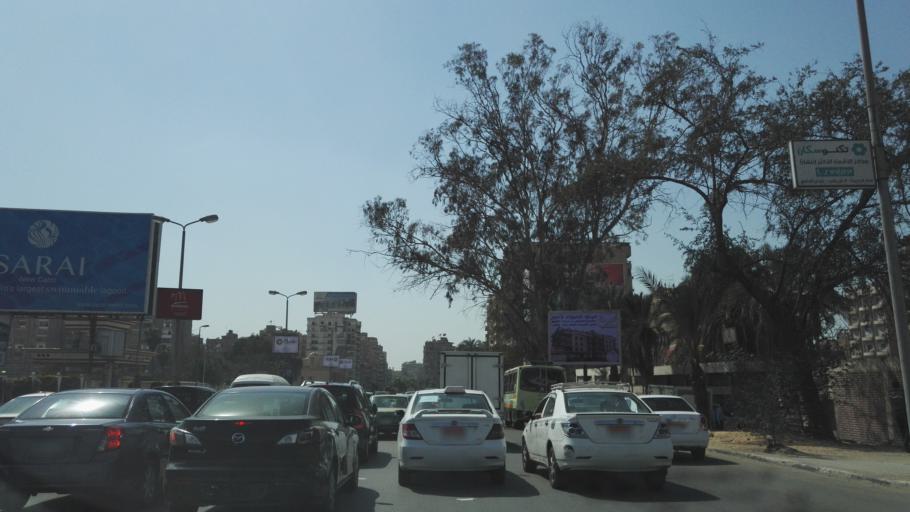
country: EG
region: Muhafazat al Qahirah
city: Cairo
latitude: 30.0815
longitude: 31.3488
